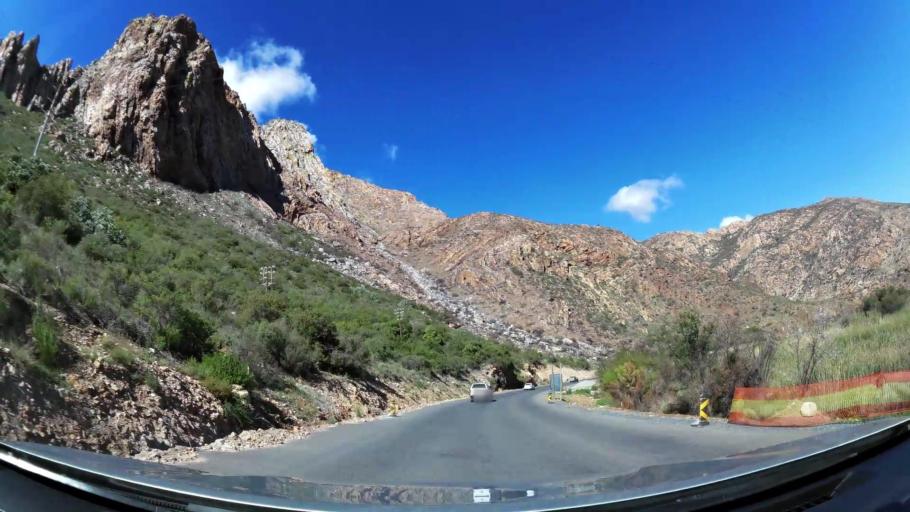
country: ZA
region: Western Cape
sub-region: Cape Winelands District Municipality
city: Ashton
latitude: -33.8002
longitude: 20.1054
